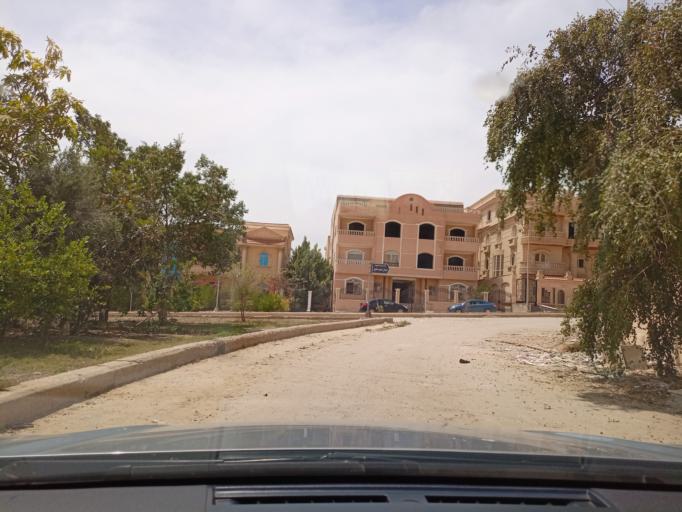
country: EG
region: Muhafazat al Qalyubiyah
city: Al Khankah
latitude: 30.2283
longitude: 31.4869
